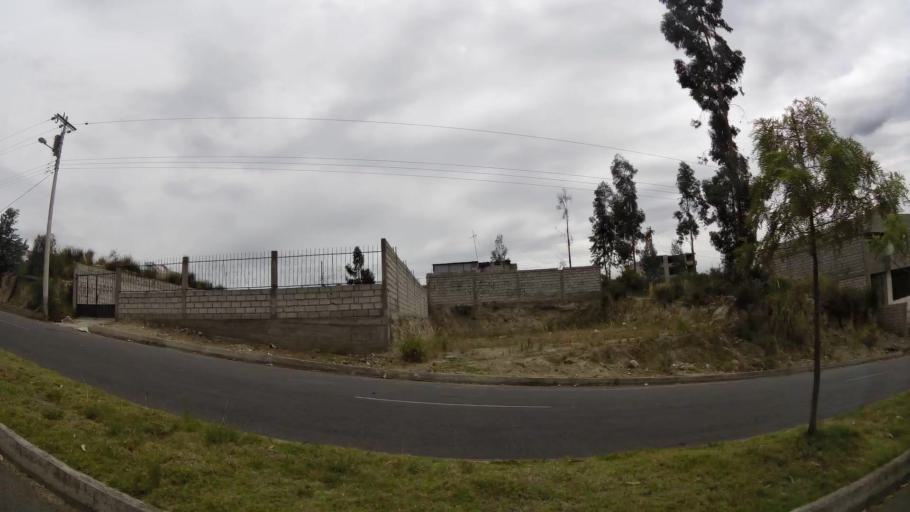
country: EC
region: Cotopaxi
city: Latacunga
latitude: -0.9489
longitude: -78.6035
